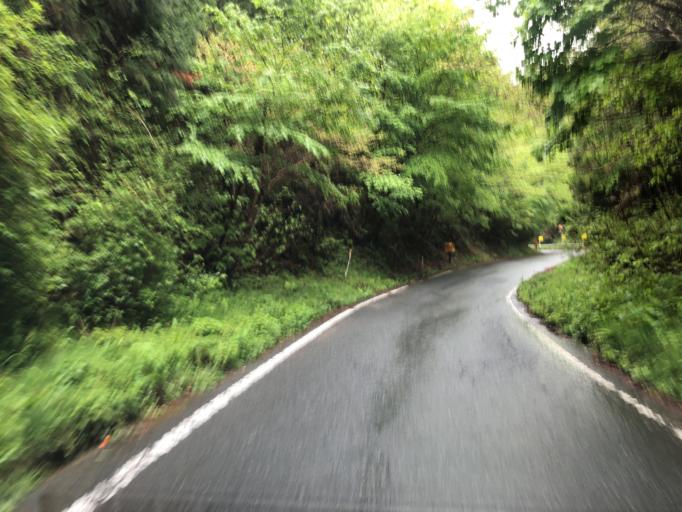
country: JP
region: Fukushima
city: Ishikawa
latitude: 37.0035
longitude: 140.5987
